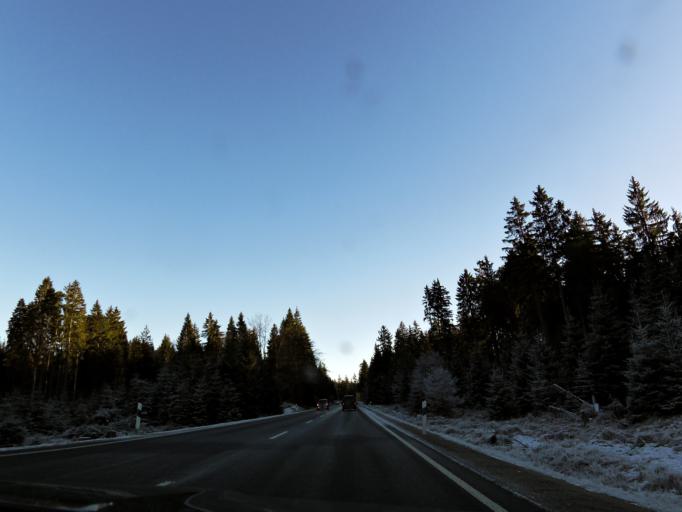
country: DE
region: Bavaria
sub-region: Upper Franconia
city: Fichtelberg
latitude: 50.0322
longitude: 11.8489
